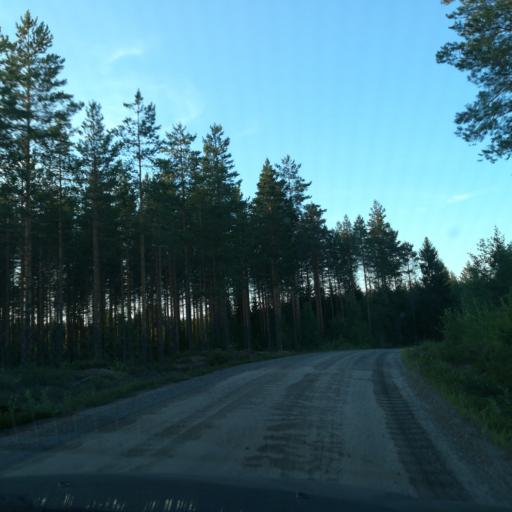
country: FI
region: Southern Savonia
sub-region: Mikkeli
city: Puumala
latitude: 61.4357
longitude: 28.4604
